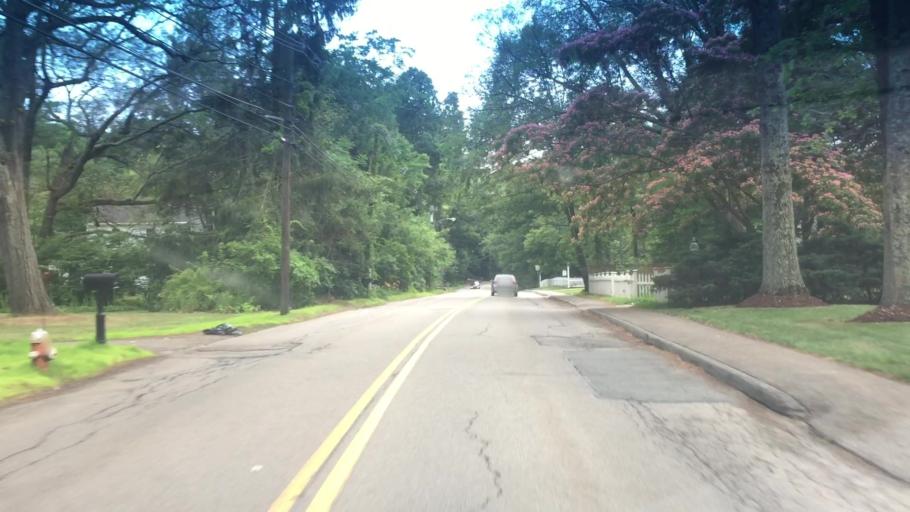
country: US
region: Massachusetts
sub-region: Norfolk County
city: Franklin
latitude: 42.0969
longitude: -71.3953
